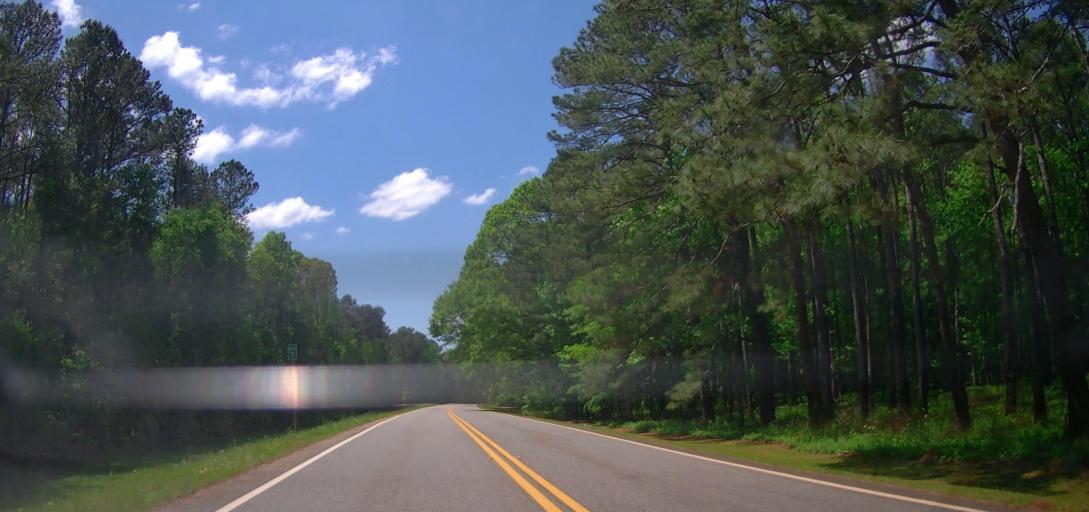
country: US
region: Georgia
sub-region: Jasper County
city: Monticello
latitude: 33.2726
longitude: -83.6640
